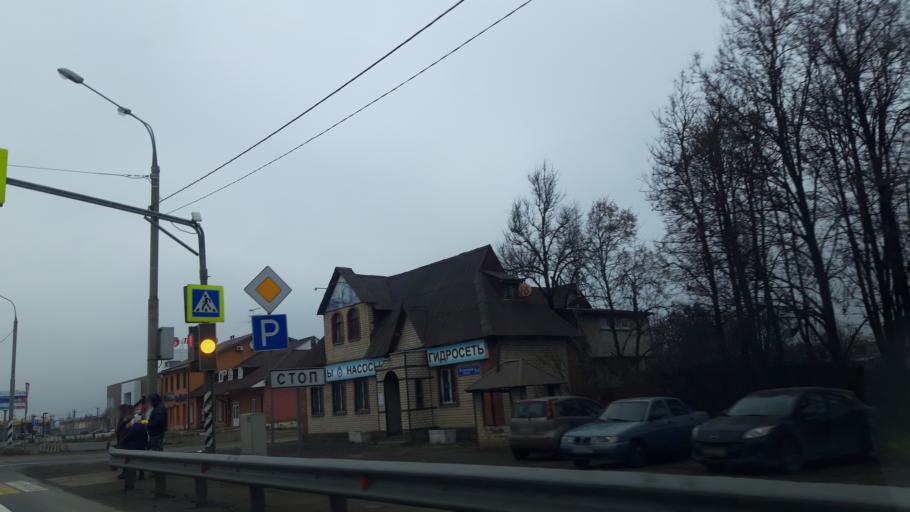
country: RU
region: Moskovskaya
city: Lozhki
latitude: 56.0979
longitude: 37.1043
